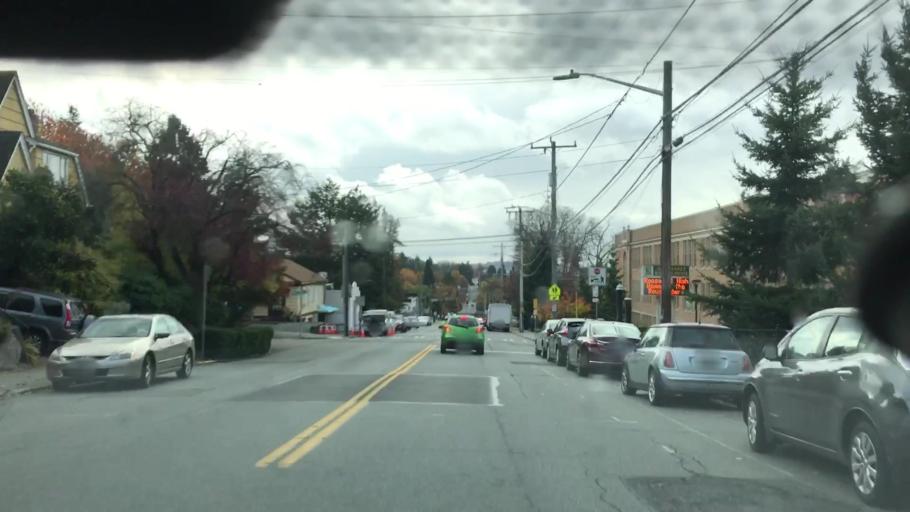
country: US
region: Washington
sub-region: King County
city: Seattle
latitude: 47.6780
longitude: -122.3120
